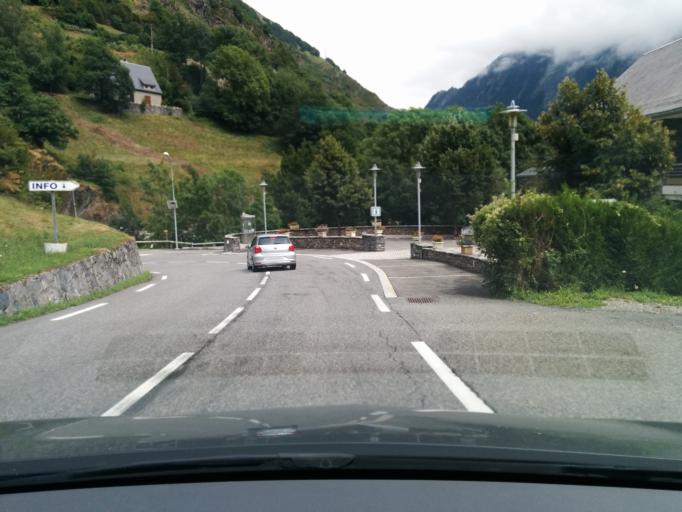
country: FR
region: Midi-Pyrenees
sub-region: Departement des Hautes-Pyrenees
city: Saint-Lary-Soulan
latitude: 42.7903
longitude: 0.2274
